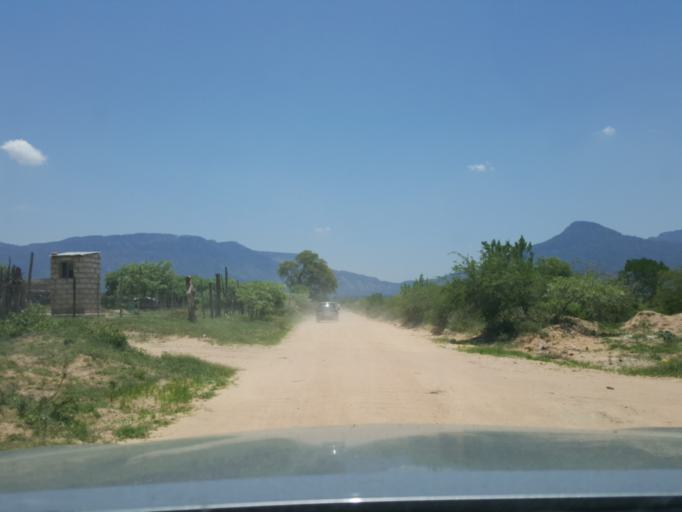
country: ZA
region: Limpopo
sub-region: Mopani District Municipality
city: Hoedspruit
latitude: -24.5845
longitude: 30.9811
